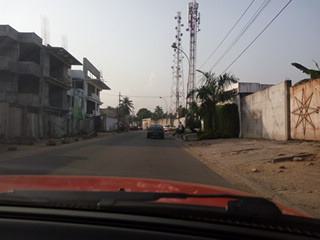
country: CI
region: Lagunes
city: Abobo
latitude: 5.3839
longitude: -3.9923
